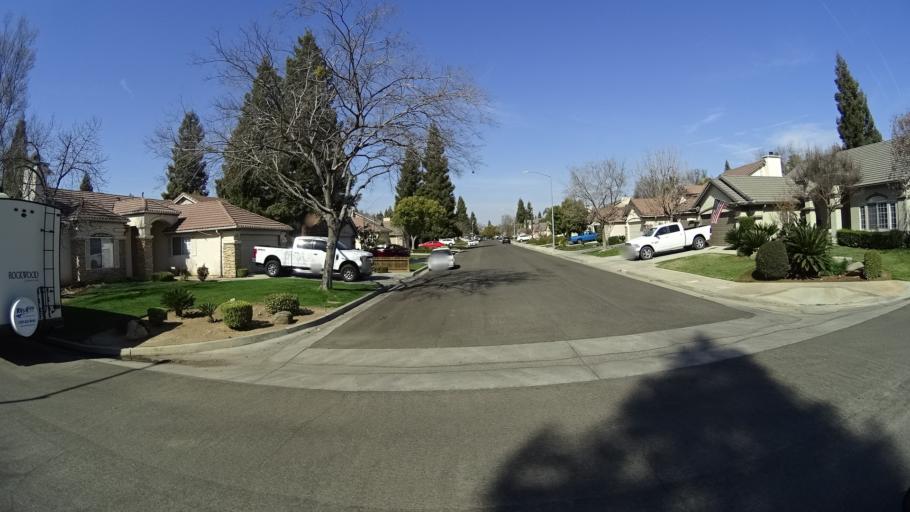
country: US
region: California
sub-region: Fresno County
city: Clovis
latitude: 36.8838
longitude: -119.7420
